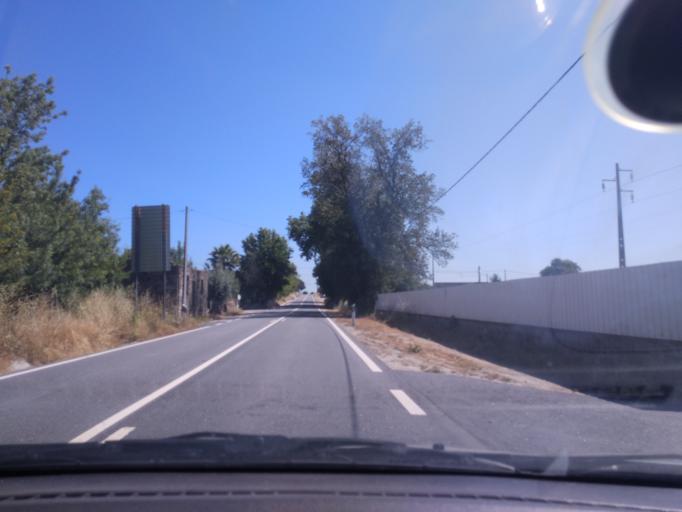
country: PT
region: Guarda
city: Alcains
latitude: 39.9253
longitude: -7.4658
